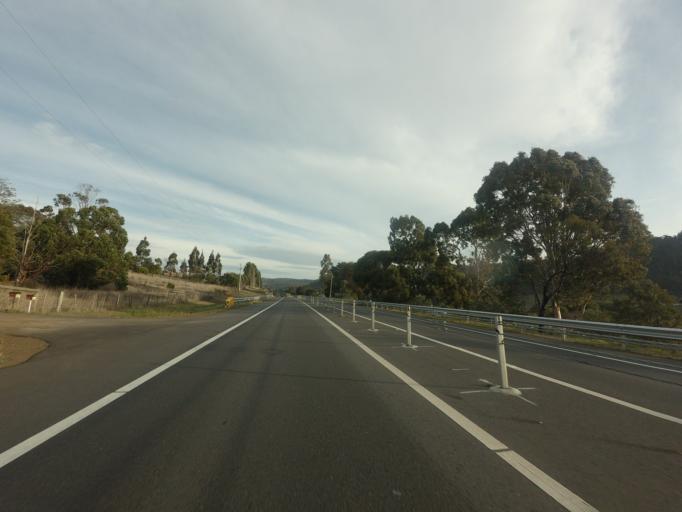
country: AU
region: Tasmania
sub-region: Brighton
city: Bridgewater
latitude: -42.5953
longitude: 147.2214
